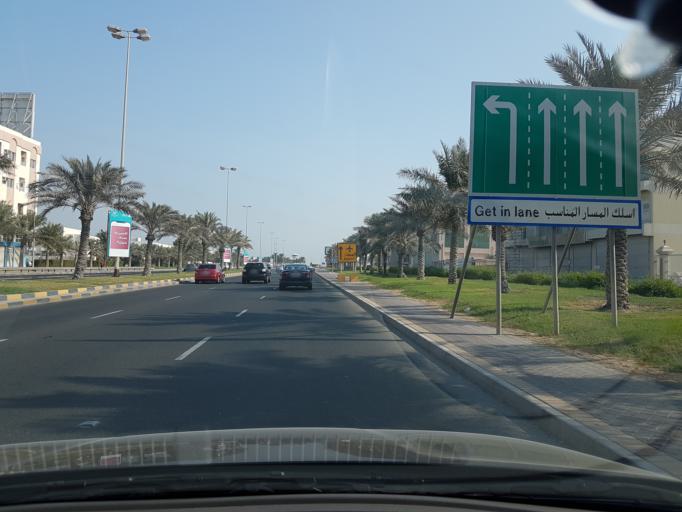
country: BH
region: Muharraq
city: Al Muharraq
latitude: 26.2473
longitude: 50.6078
